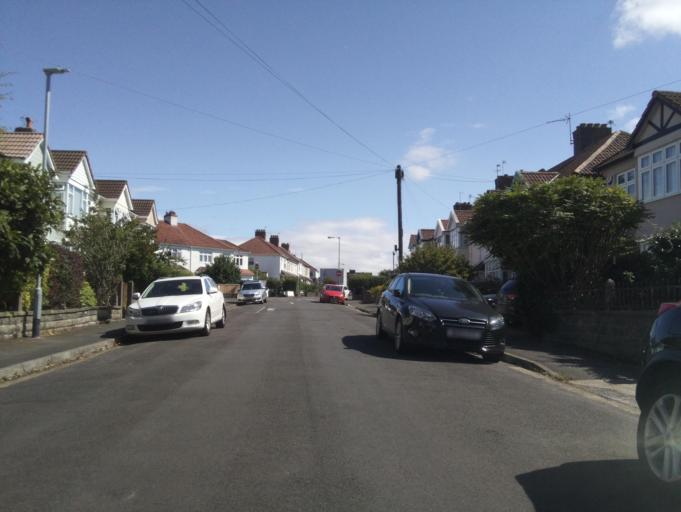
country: GB
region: England
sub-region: Bristol
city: Bristol
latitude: 51.4955
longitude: -2.6033
